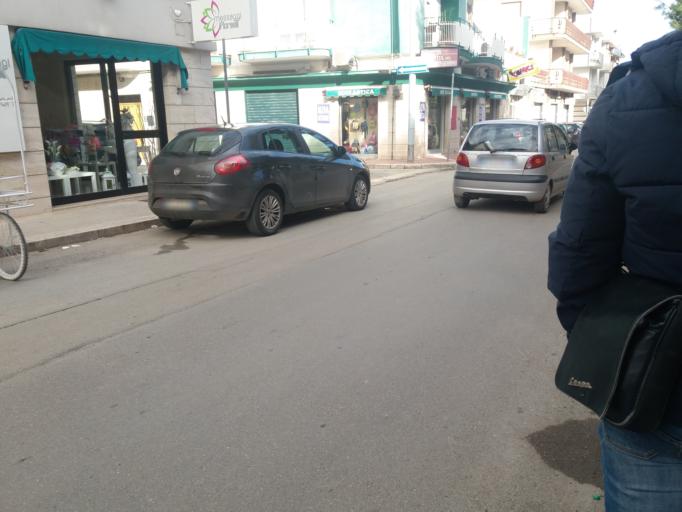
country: IT
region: Apulia
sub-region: Provincia di Barletta - Andria - Trani
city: Andria
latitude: 41.2372
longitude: 16.2995
